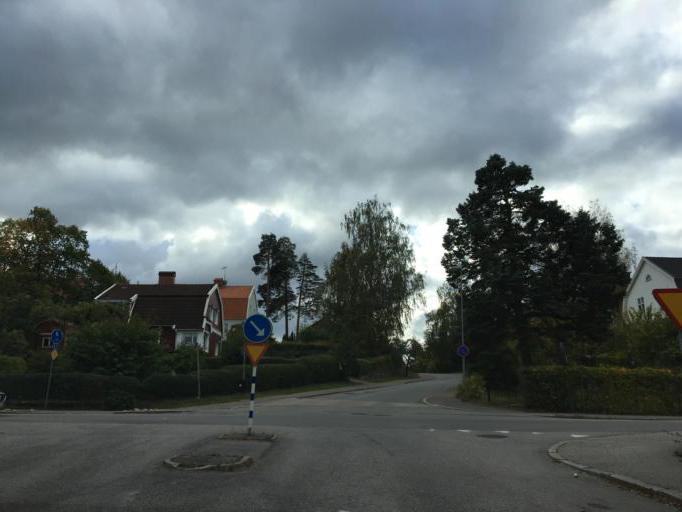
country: SE
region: Soedermanland
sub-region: Katrineholms Kommun
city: Katrineholm
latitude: 58.9922
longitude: 16.2008
